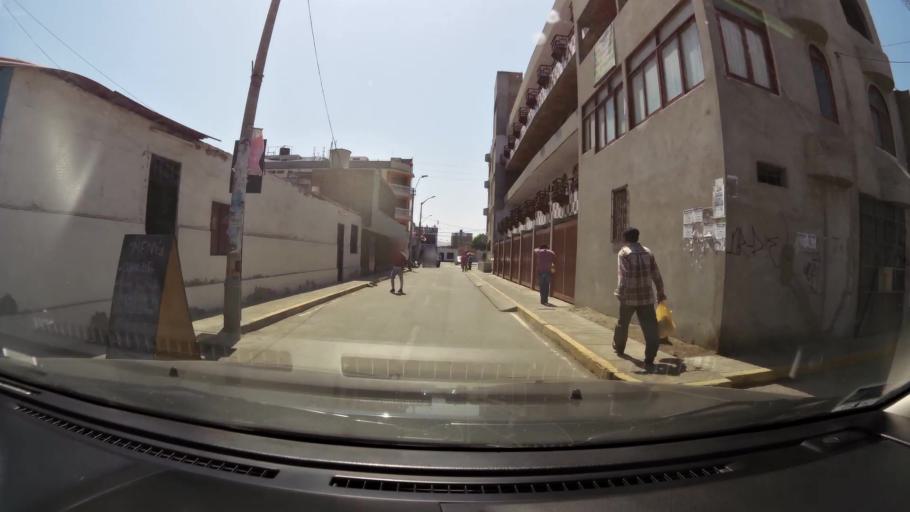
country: PE
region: Lima
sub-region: Provincia de Canete
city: San Vicente de Canete
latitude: -13.0257
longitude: -76.4795
